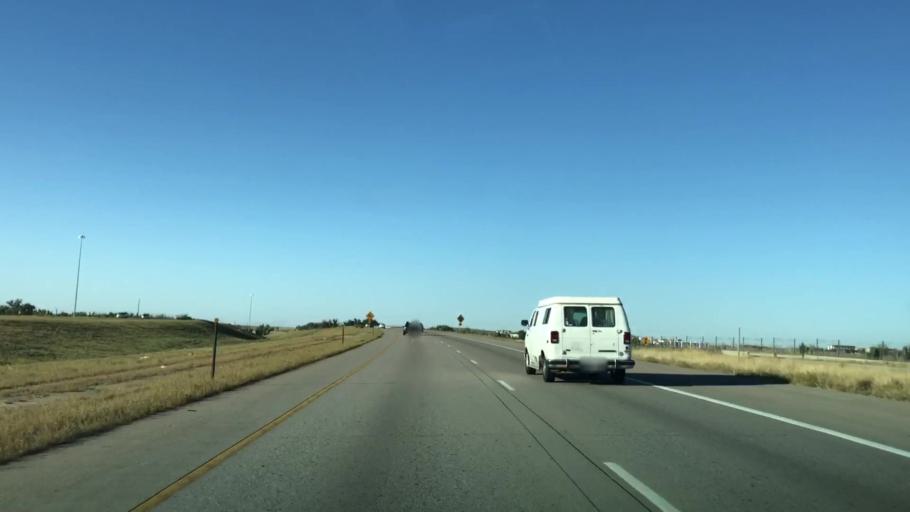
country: US
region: Colorado
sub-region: Adams County
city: Aurora
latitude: 39.7950
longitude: -104.7870
